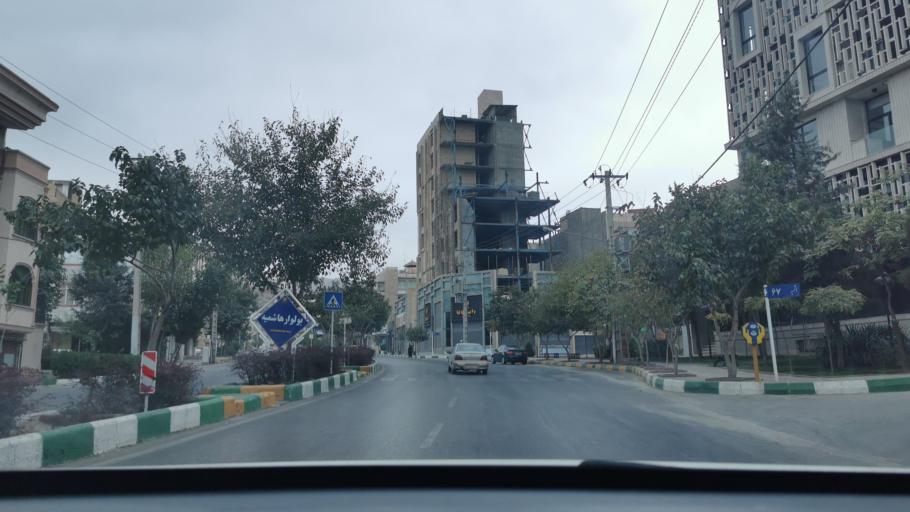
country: IR
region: Razavi Khorasan
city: Mashhad
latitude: 36.3054
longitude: 59.4997
